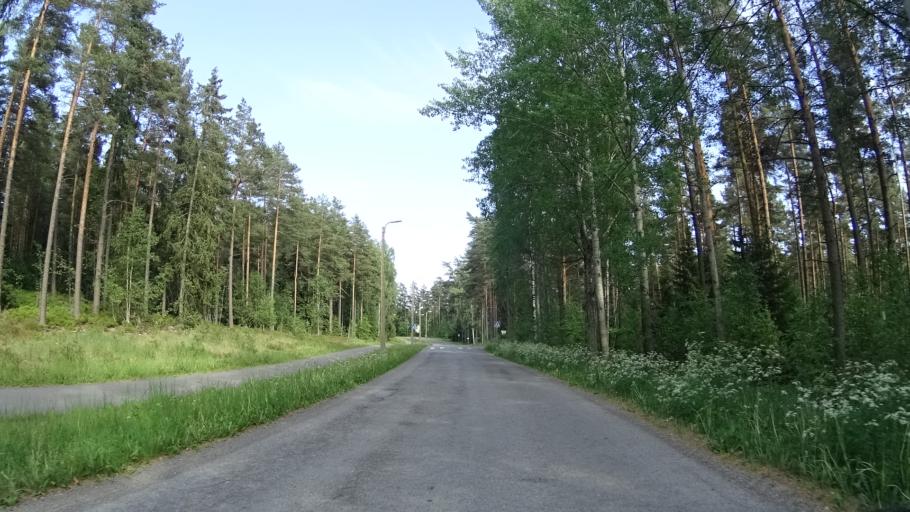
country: FI
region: Uusimaa
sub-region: Raaseporin
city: Inga
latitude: 60.0550
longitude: 23.9843
